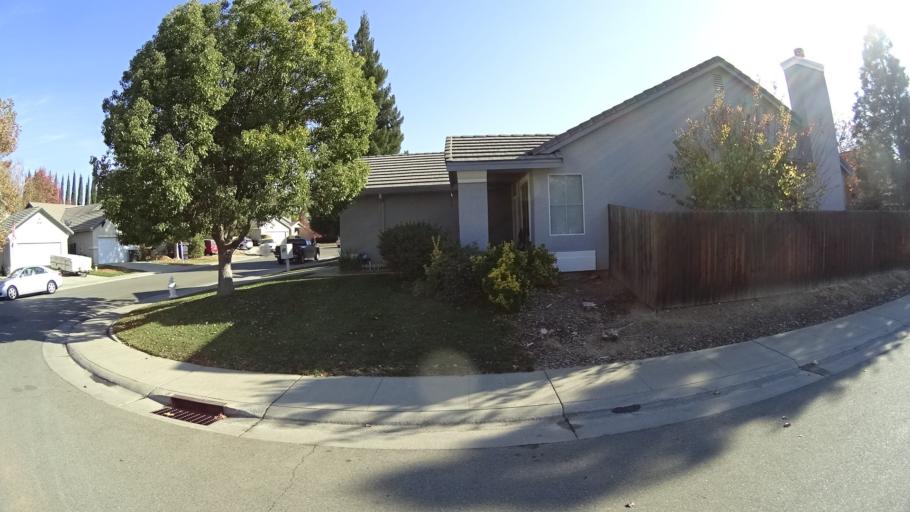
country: US
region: California
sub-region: Sacramento County
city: Citrus Heights
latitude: 38.6845
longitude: -121.2990
